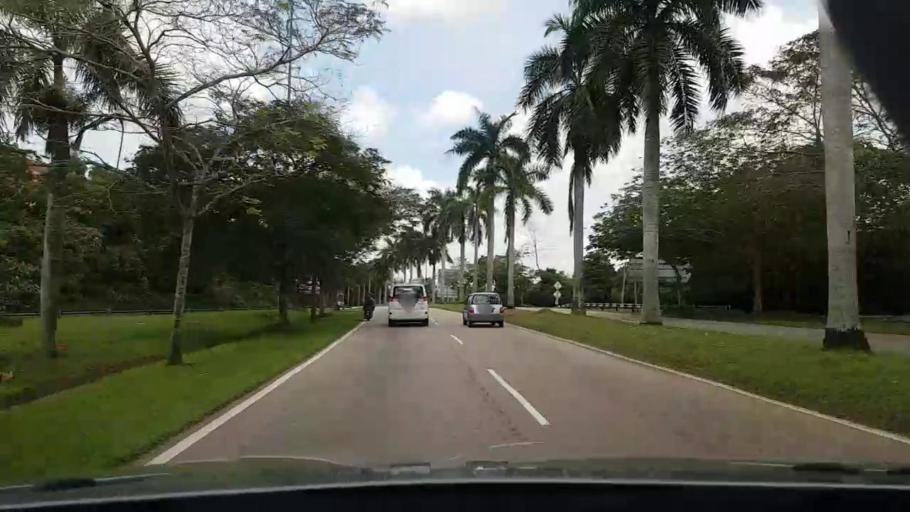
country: MY
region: Pahang
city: Kuantan
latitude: 3.8365
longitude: 103.2886
